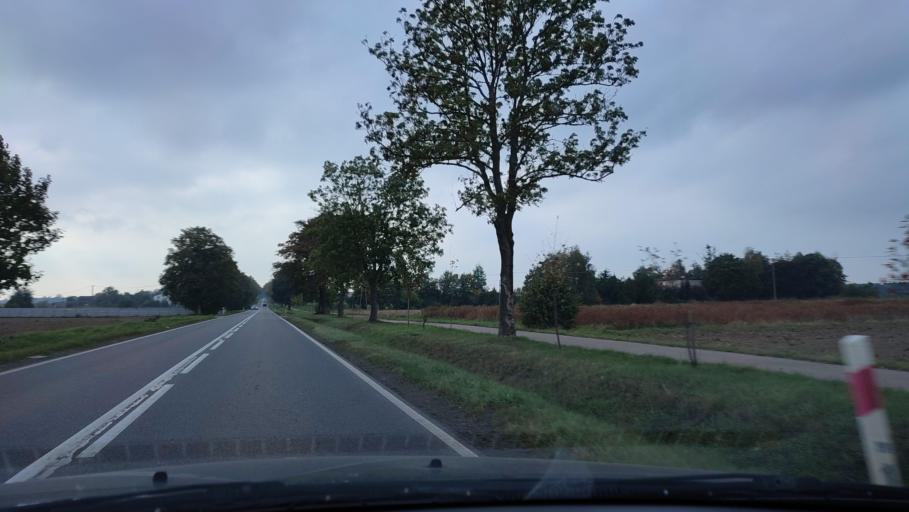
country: PL
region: Warmian-Masurian Voivodeship
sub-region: Powiat nidzicki
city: Nidzica
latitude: 53.3537
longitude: 20.3730
